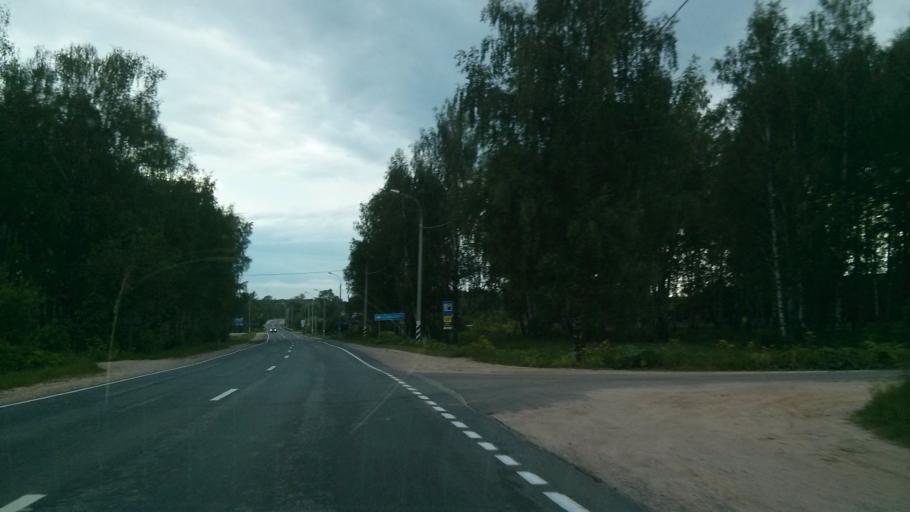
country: RU
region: Nizjnij Novgorod
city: Vacha
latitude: 55.7582
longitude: 42.5230
